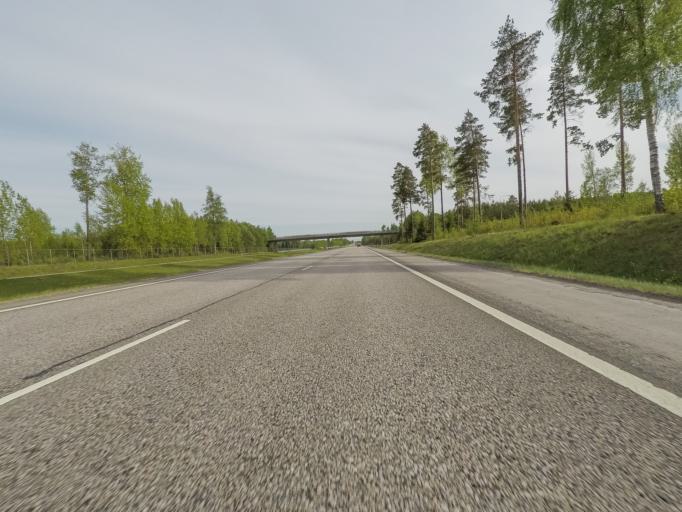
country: FI
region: Uusimaa
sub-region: Helsinki
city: Nurmijaervi
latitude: 60.5178
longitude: 24.8458
